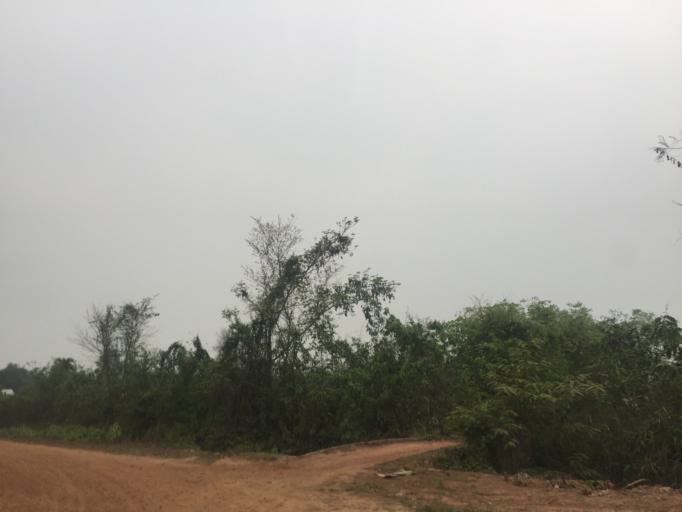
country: LA
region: Xiagnabouli
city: Sainyabuli
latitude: 19.0038
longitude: 101.5155
